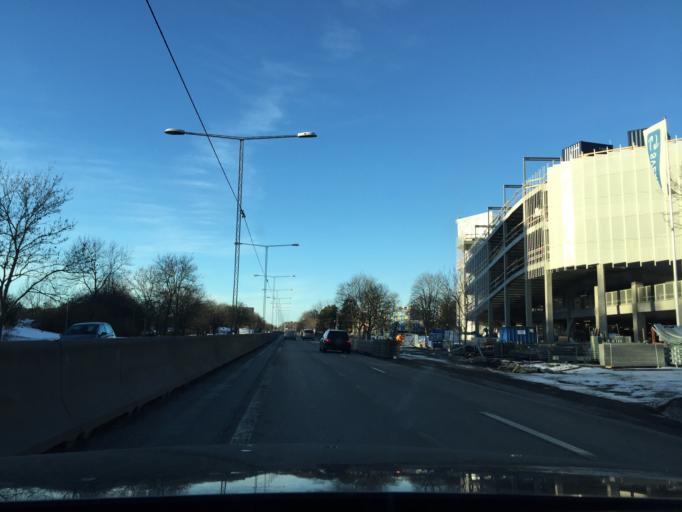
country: SE
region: Stockholm
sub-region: Stockholms Kommun
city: Bromma
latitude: 59.3538
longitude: 17.8816
